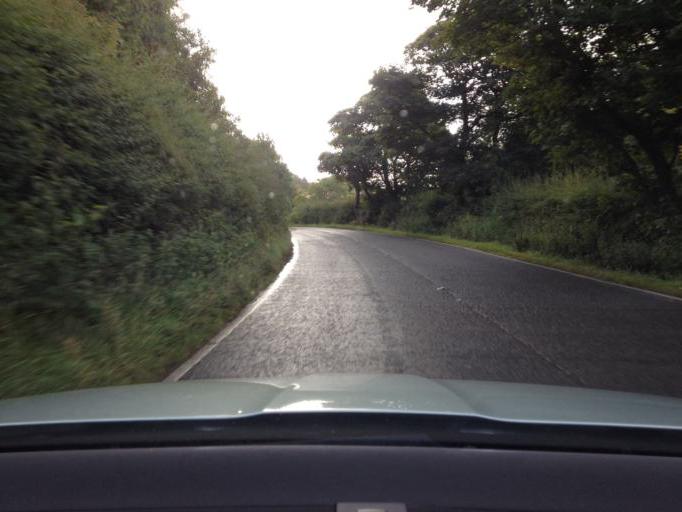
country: GB
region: Scotland
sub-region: West Lothian
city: West Calder
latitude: 55.8271
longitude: -3.5372
